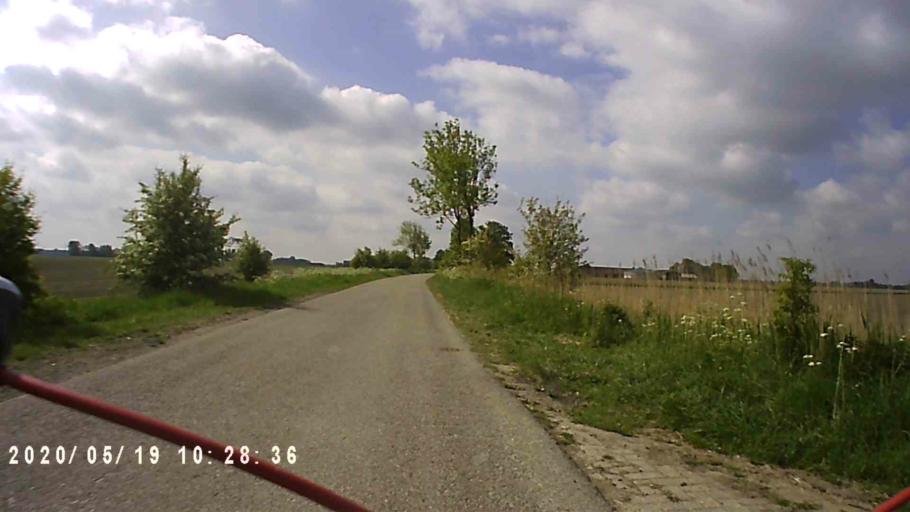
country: NL
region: Friesland
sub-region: Gemeente Kollumerland en Nieuwkruisland
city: Kollum
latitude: 53.3017
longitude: 6.1963
